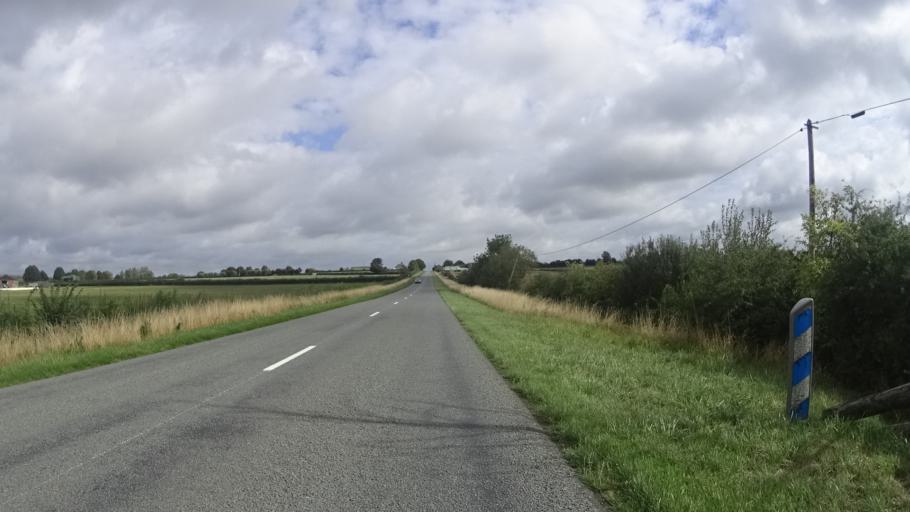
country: FR
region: Picardie
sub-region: Departement de l'Aisne
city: Boue
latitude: 50.0433
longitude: 3.6644
